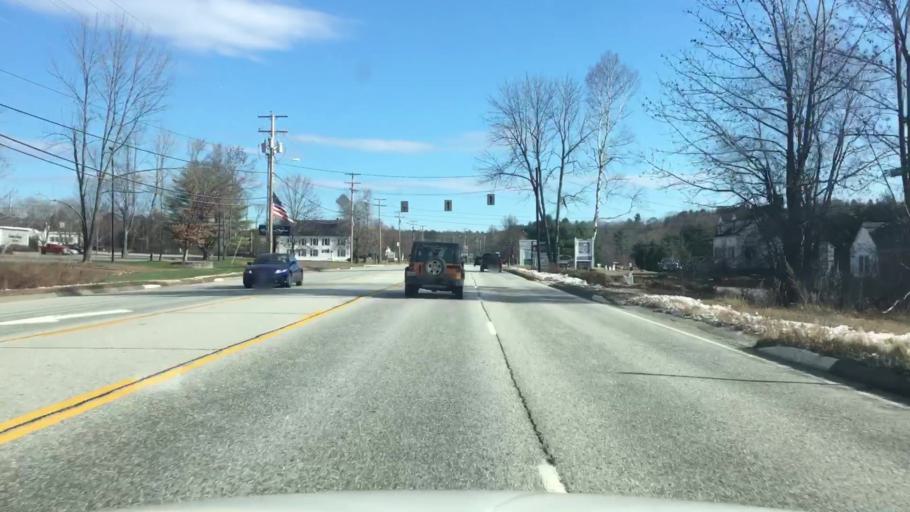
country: US
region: Maine
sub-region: Kennebec County
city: Manchester
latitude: 44.3238
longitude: -69.8671
